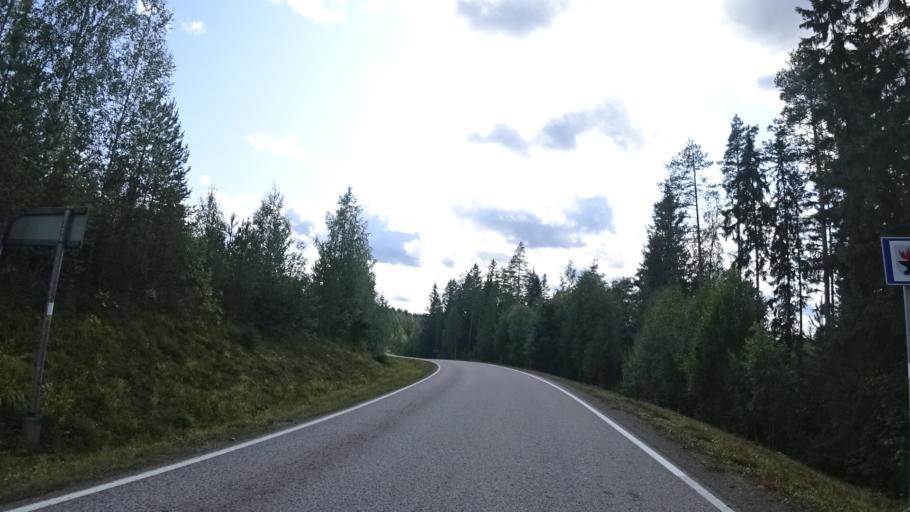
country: RU
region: Republic of Karelia
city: Vyartsilya
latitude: 62.2651
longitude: 30.7773
